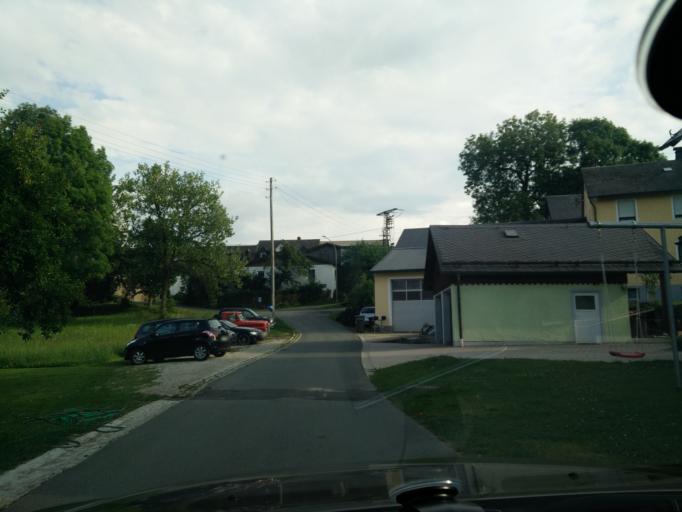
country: DE
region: Bavaria
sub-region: Upper Franconia
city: Roslau
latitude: 50.0786
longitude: 11.9598
